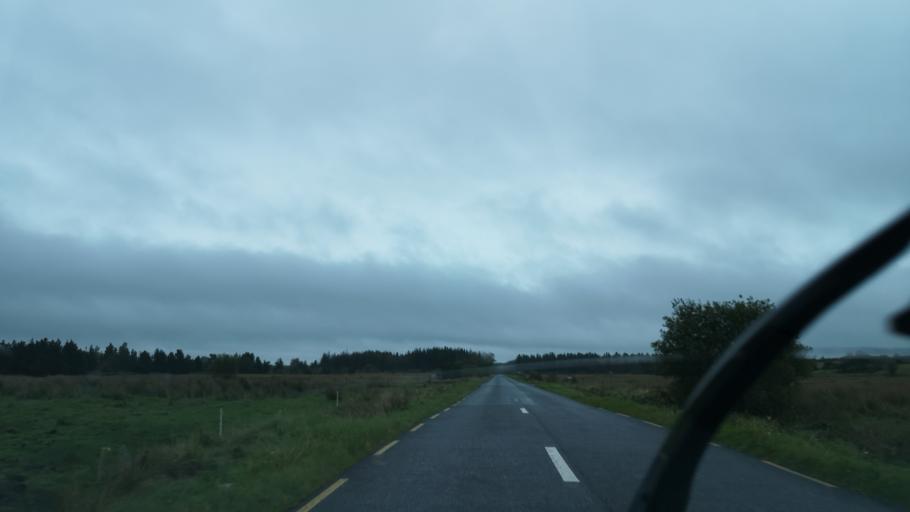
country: IE
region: Connaught
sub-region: Roscommon
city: Ballaghaderreen
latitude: 53.8144
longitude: -8.6500
